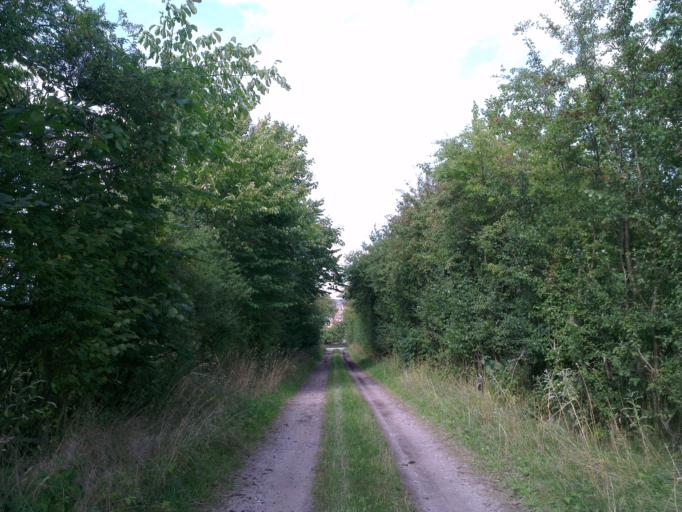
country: DK
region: Capital Region
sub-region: Frederikssund Kommune
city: Jaegerspris
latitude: 55.8539
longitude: 11.9738
